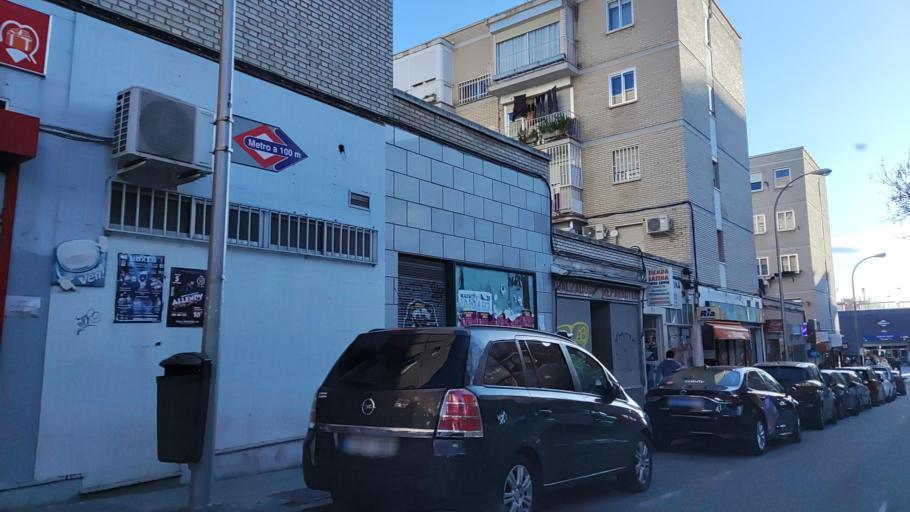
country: ES
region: Madrid
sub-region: Provincia de Madrid
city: Latina
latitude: 40.3977
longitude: -3.7730
